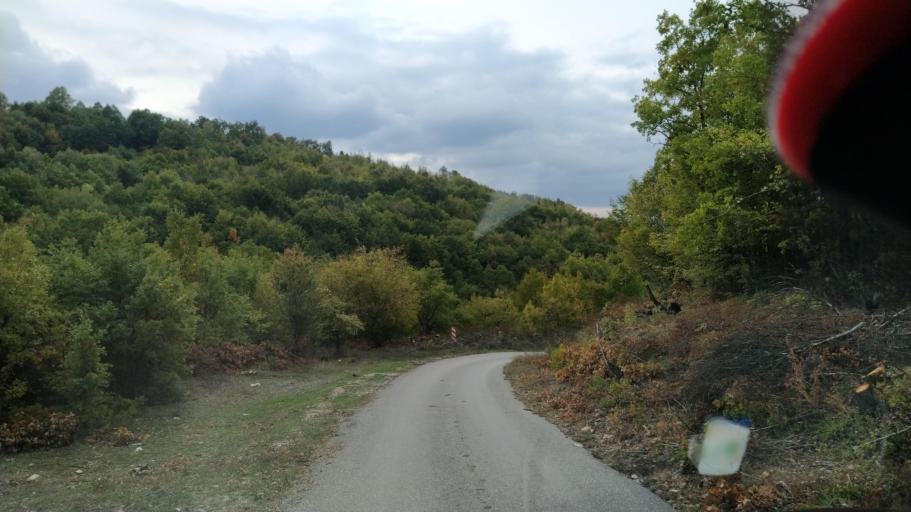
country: MK
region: Strumica
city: Veljusa
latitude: 41.5106
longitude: 22.4872
